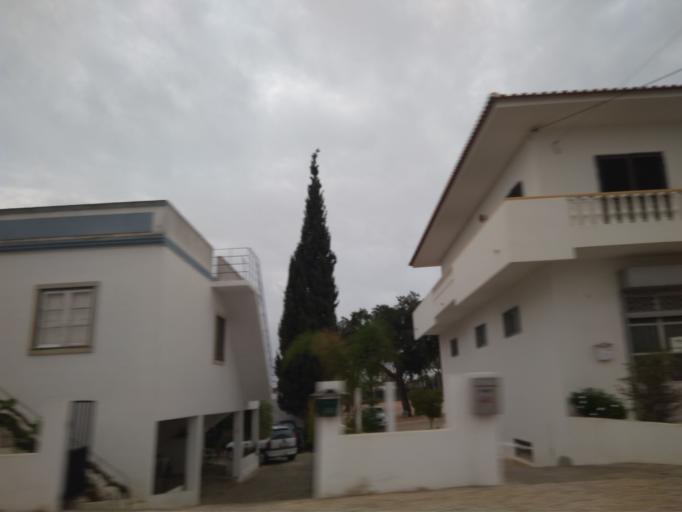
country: PT
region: Faro
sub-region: Faro
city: Faro
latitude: 37.0299
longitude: -7.9699
